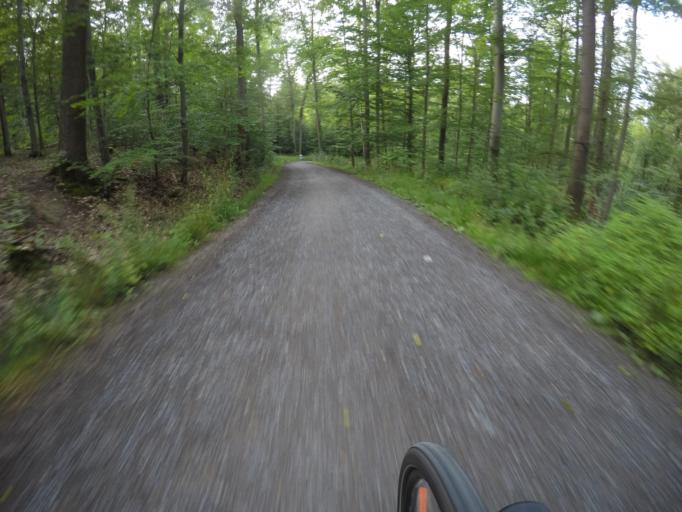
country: DE
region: Baden-Wuerttemberg
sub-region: Regierungsbezirk Stuttgart
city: Gerlingen
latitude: 48.7535
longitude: 9.1016
